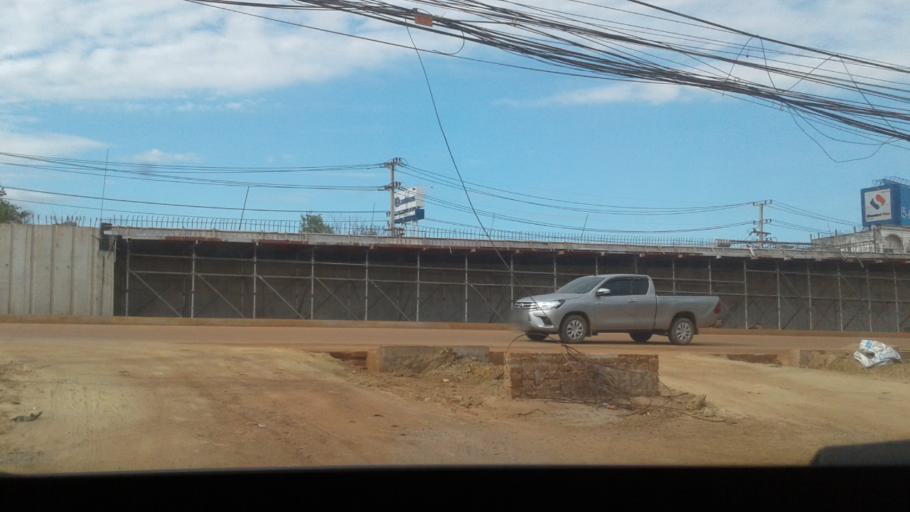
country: TH
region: Changwat Udon Thani
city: Udon Thani
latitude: 17.4340
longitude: 102.7900
